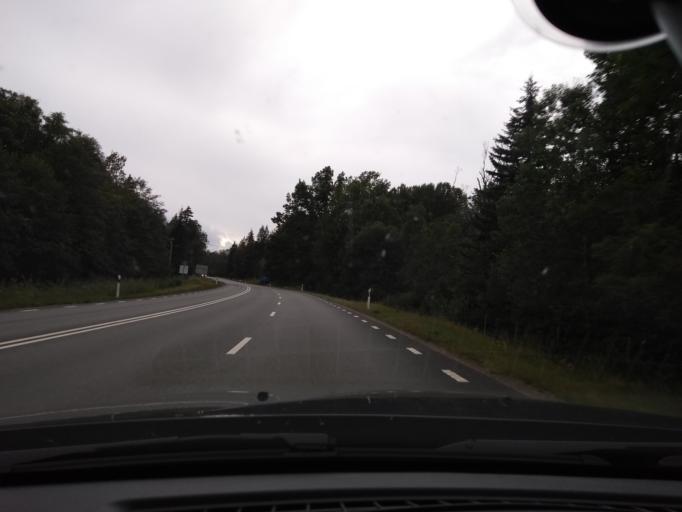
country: SE
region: Joenkoeping
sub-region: Eksjo Kommun
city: Eksjoe
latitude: 57.6358
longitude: 14.8627
